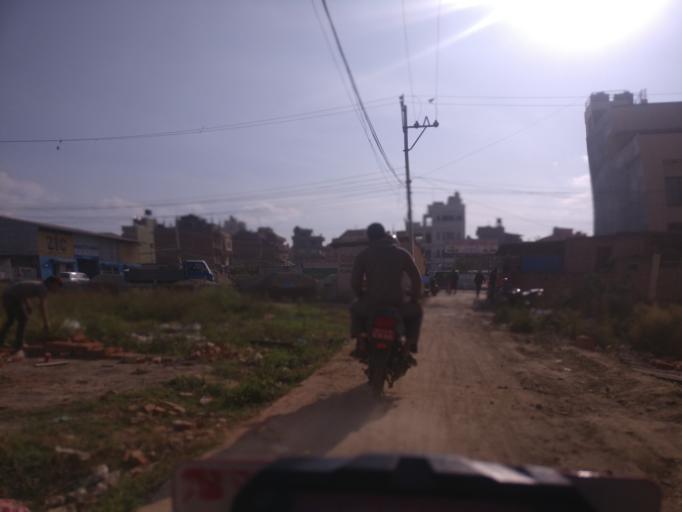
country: NP
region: Central Region
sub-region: Bagmati Zone
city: Patan
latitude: 27.6809
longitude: 85.3284
